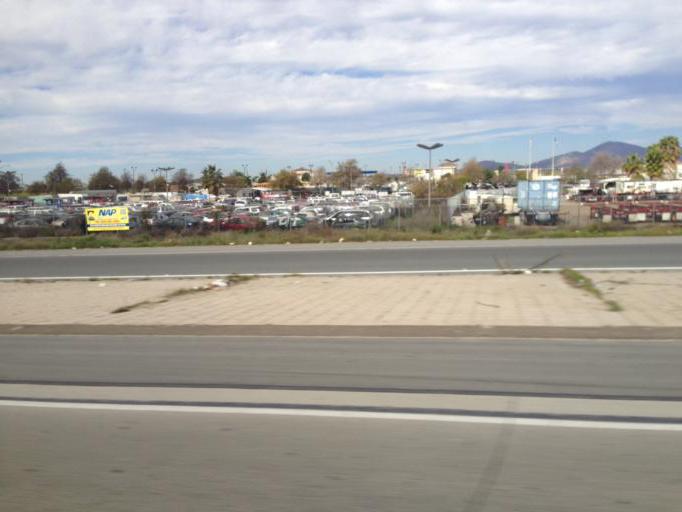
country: MX
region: Baja California
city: Tijuana
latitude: 32.5644
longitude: -116.9650
